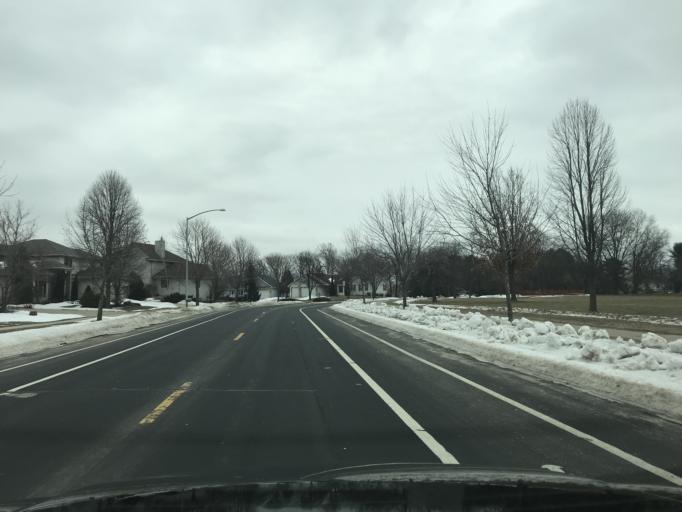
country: US
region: Wisconsin
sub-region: Dane County
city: Monona
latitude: 43.0796
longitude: -89.2733
